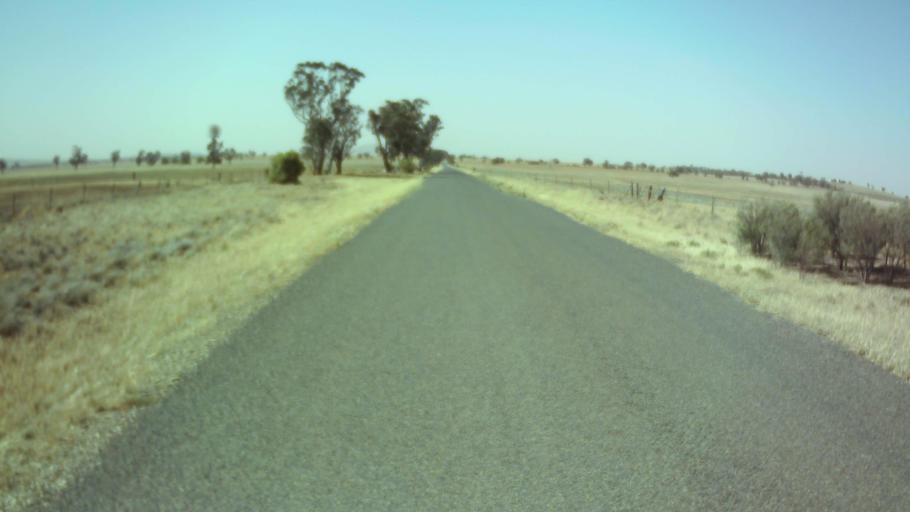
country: AU
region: New South Wales
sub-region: Weddin
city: Grenfell
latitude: -33.8744
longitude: 147.9257
